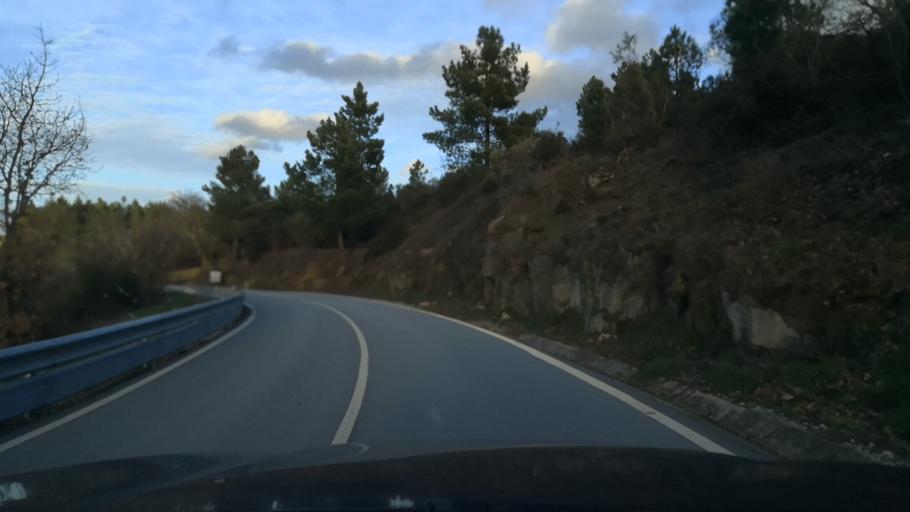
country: PT
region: Braganca
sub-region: Carrazeda de Ansiaes
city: Carrazeda de Anciaes
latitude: 41.2107
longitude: -7.3292
